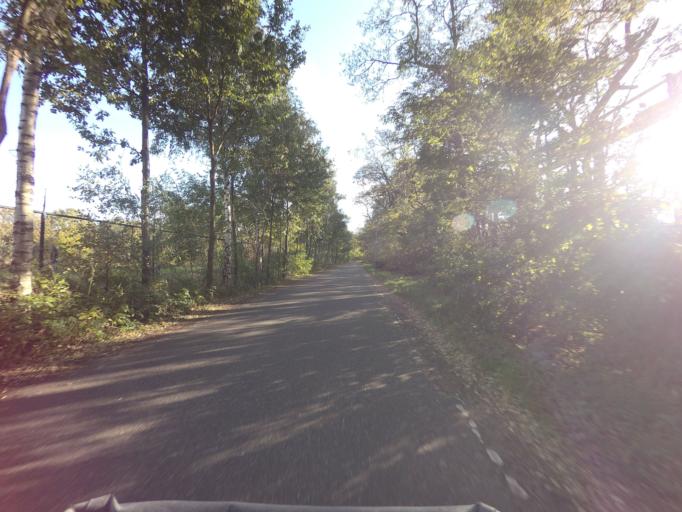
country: NL
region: North Holland
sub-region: Gemeente Bussum
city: Bussum
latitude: 52.2540
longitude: 5.1695
